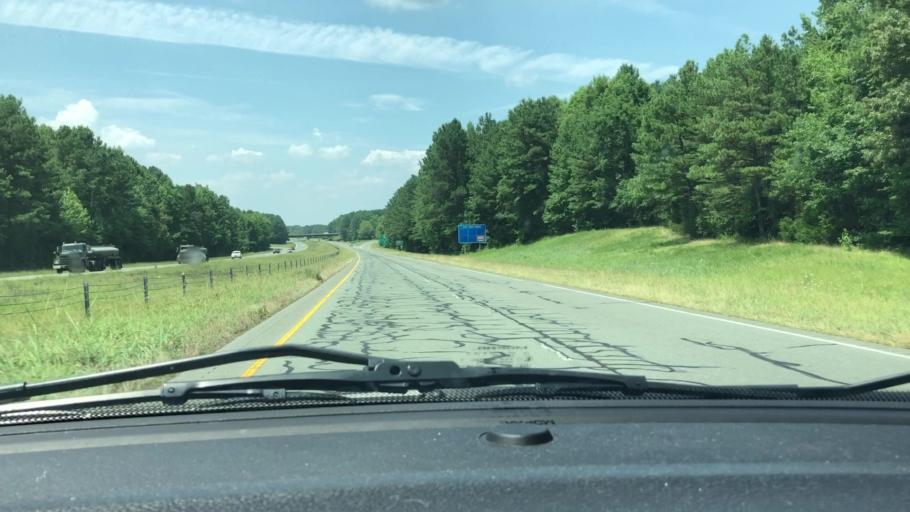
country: US
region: North Carolina
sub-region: Chatham County
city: Siler City
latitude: 35.7262
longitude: -79.4299
